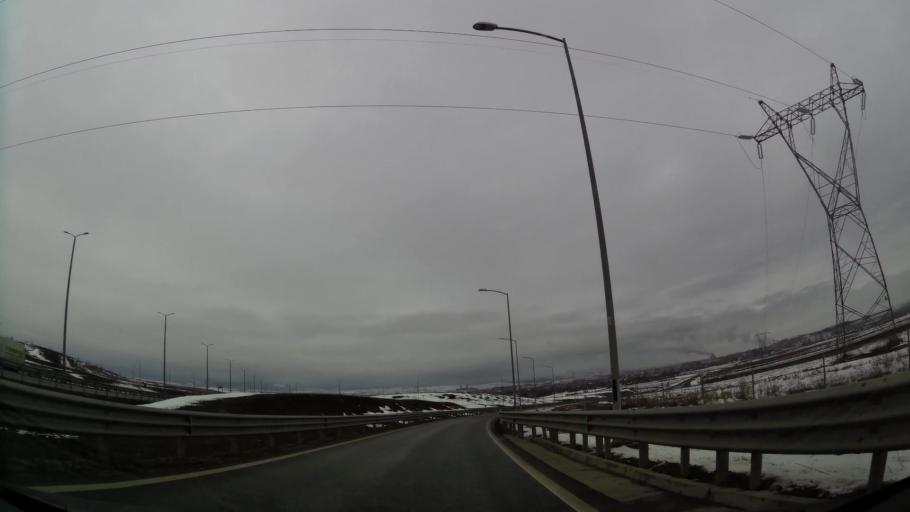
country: XK
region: Pristina
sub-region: Kosovo Polje
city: Kosovo Polje
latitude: 42.6196
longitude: 21.1199
